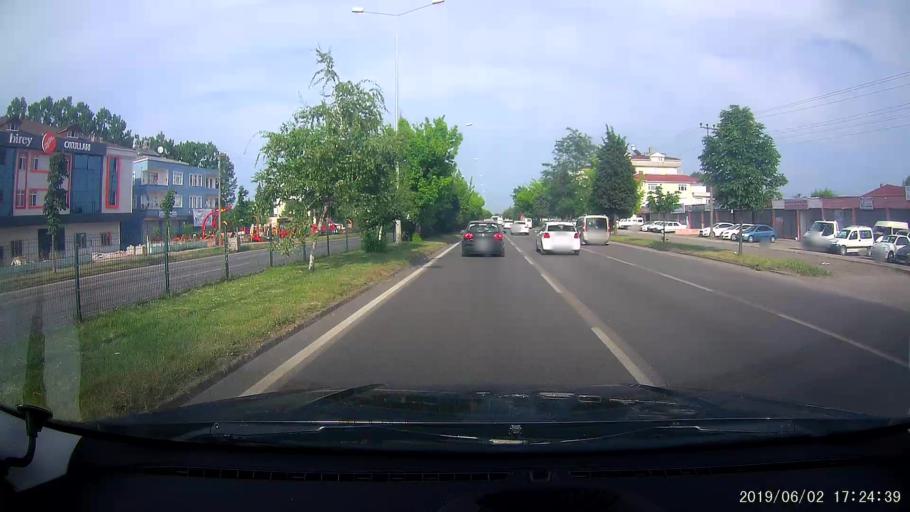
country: TR
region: Samsun
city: Carsamba
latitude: 41.2053
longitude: 36.7049
